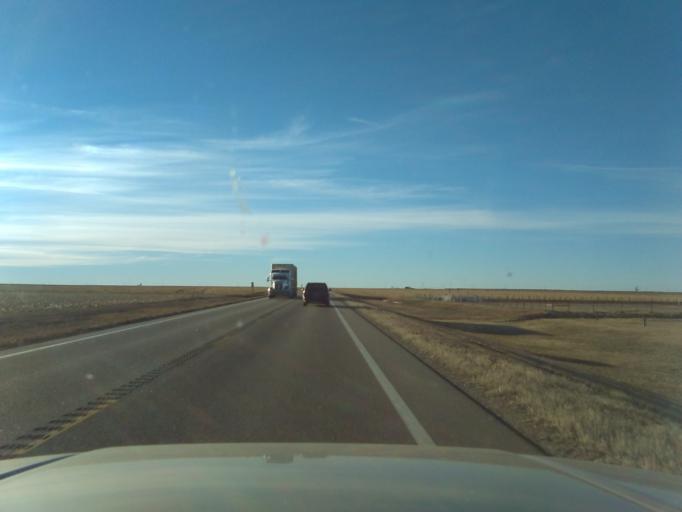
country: US
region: Kansas
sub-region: Thomas County
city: Colby
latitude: 39.4649
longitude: -100.7433
